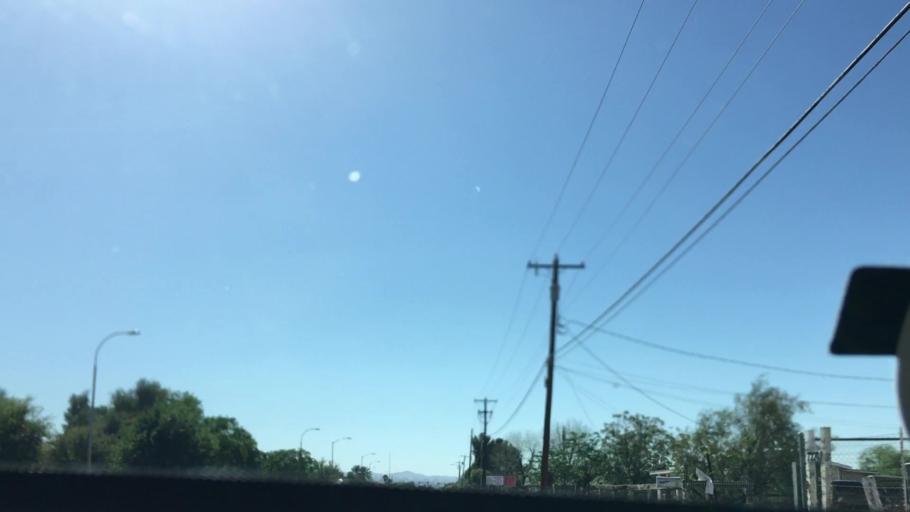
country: US
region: Arizona
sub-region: Maricopa County
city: Peoria
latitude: 33.6105
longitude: -112.2142
